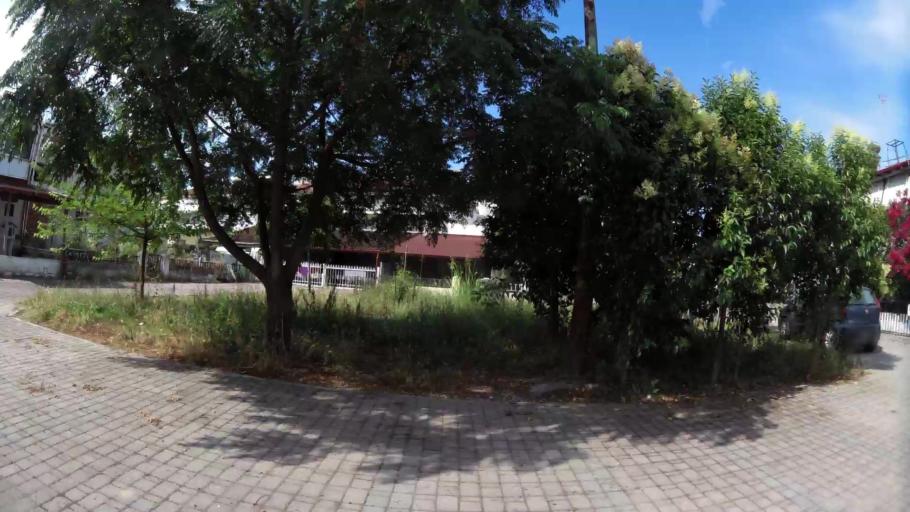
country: GR
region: Central Macedonia
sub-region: Nomos Pierias
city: Katerini
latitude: 40.2852
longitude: 22.5172
